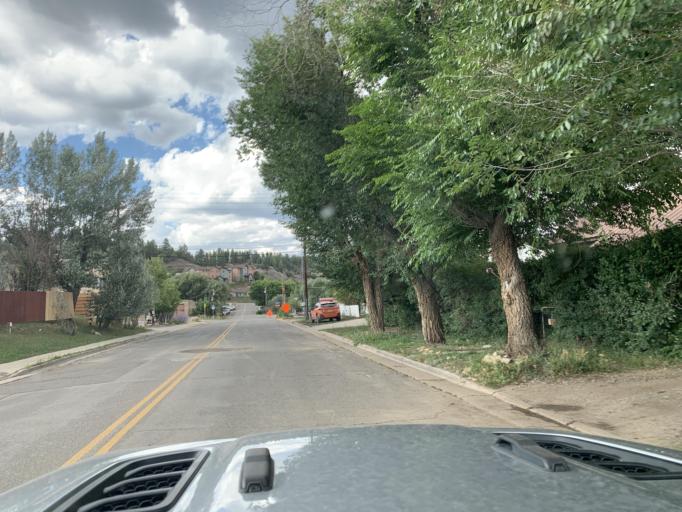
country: US
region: Colorado
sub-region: Archuleta County
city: Pagosa Springs
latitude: 37.2653
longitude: -107.0158
